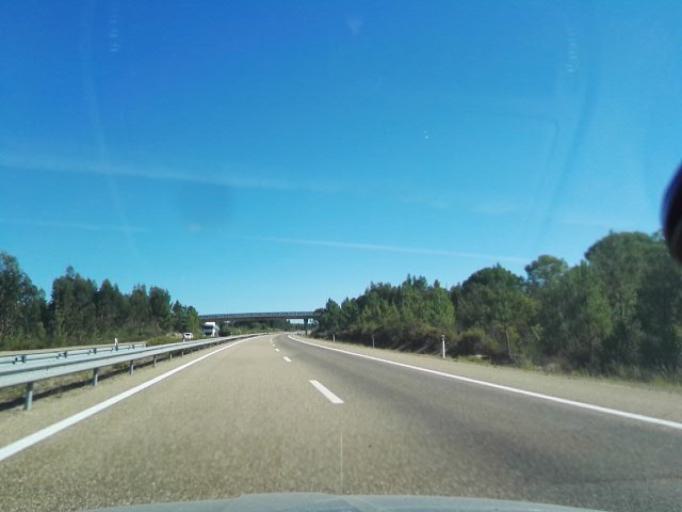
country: PT
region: Evora
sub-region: Vendas Novas
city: Vendas Novas
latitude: 38.6562
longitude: -8.6629
